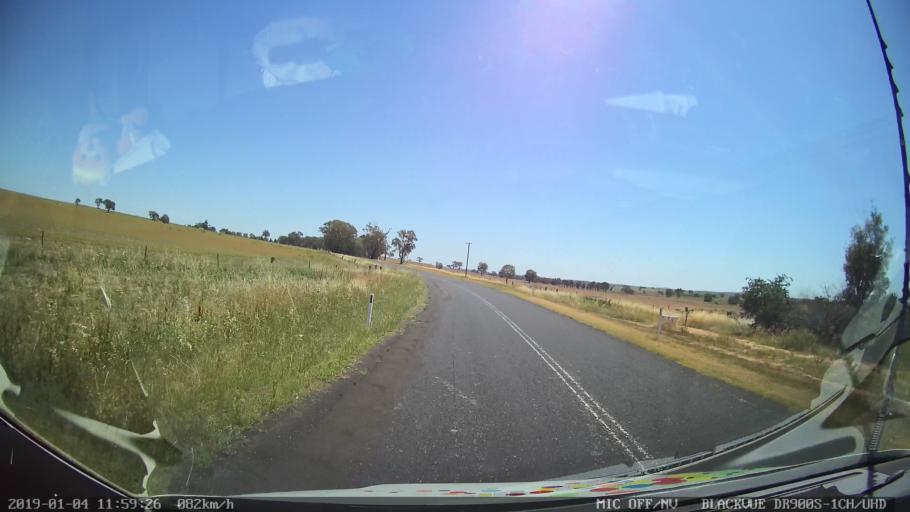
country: AU
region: New South Wales
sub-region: Cabonne
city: Molong
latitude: -32.8139
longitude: 148.6957
